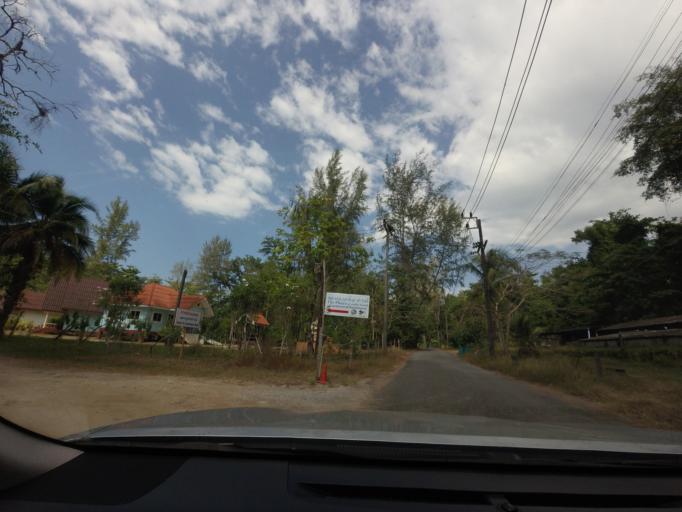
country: TH
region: Phangnga
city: Ban Khao Lak
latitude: 8.7371
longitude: 98.2437
